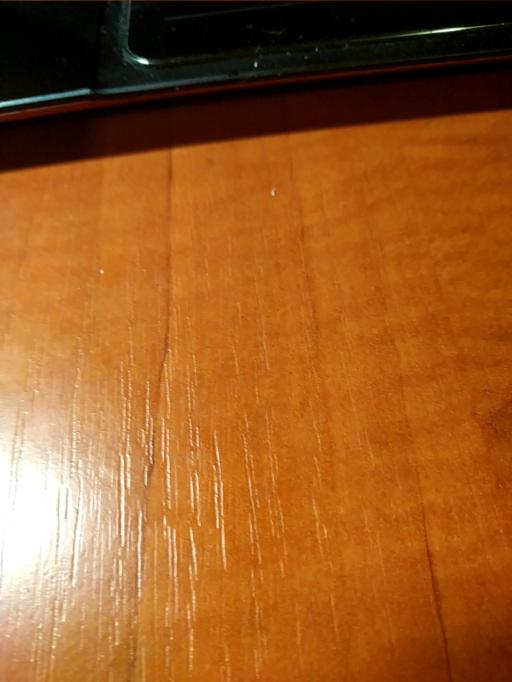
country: RU
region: Tverskaya
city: Vyshniy Volochek
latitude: 57.4061
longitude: 34.5121
